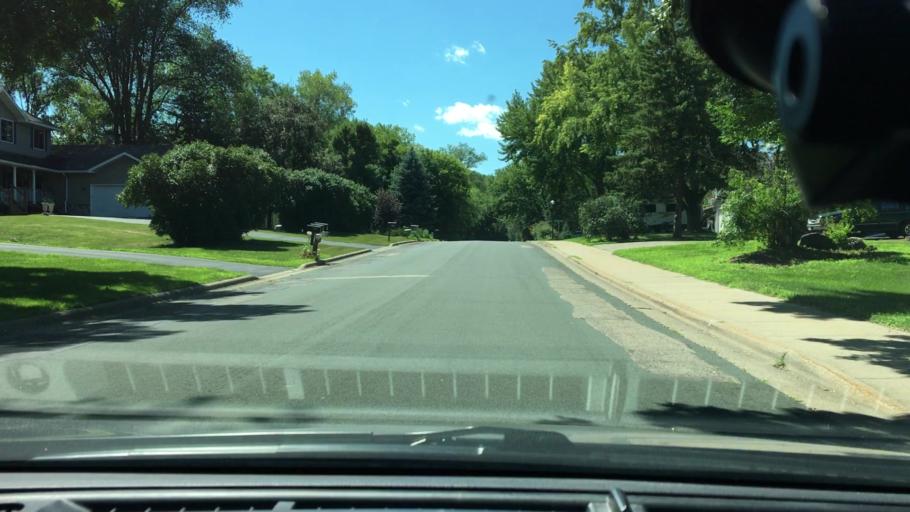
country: US
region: Minnesota
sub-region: Hennepin County
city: Maple Grove
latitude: 45.0694
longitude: -93.4551
